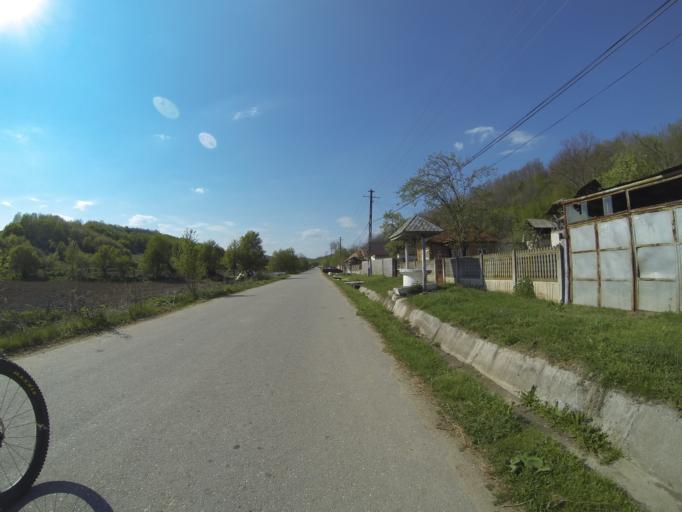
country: RO
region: Gorj
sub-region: Comuna Crusetu
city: Crusetu
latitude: 44.6258
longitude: 23.6332
